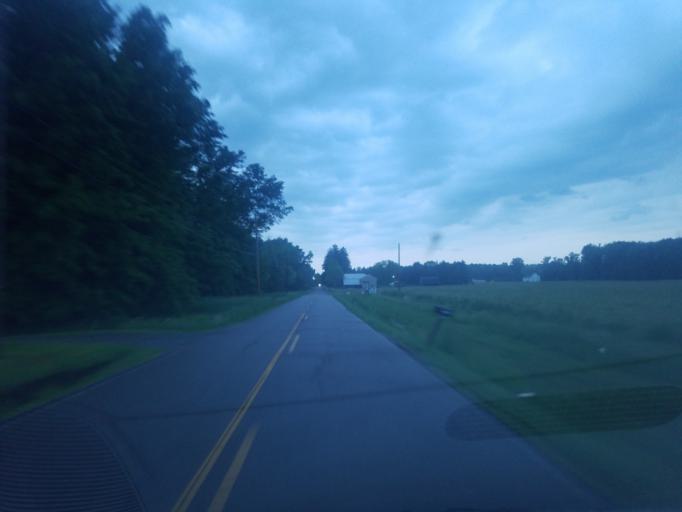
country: US
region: Ohio
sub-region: Mahoning County
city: Canfield
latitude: 40.9727
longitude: -80.7769
